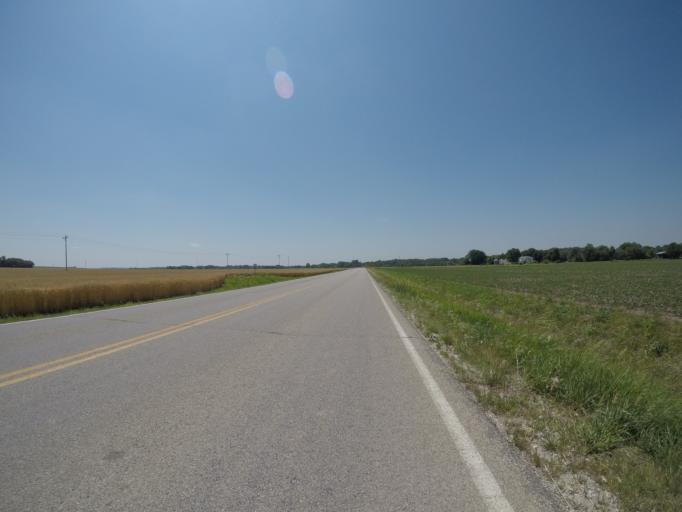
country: US
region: Kansas
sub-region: Pottawatomie County
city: Westmoreland
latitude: 39.2927
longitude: -96.4406
